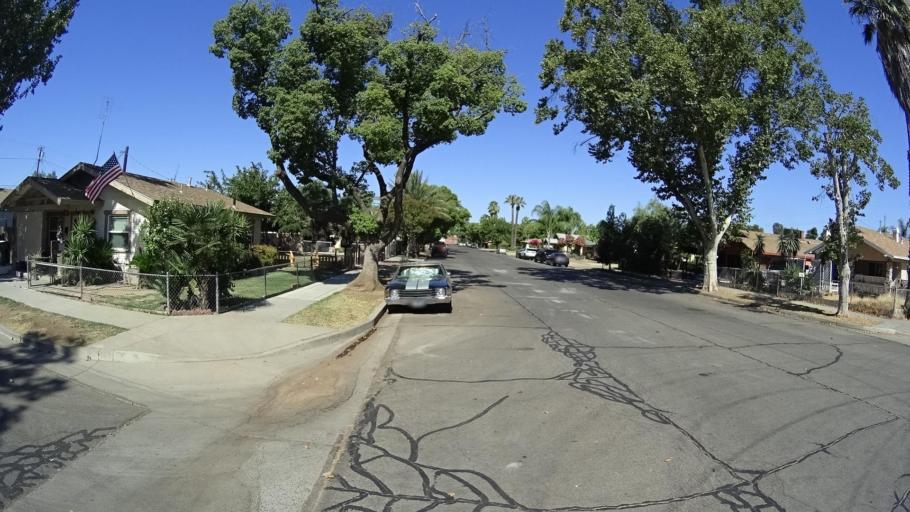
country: US
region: California
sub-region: Fresno County
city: Fresno
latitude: 36.7307
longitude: -119.7677
